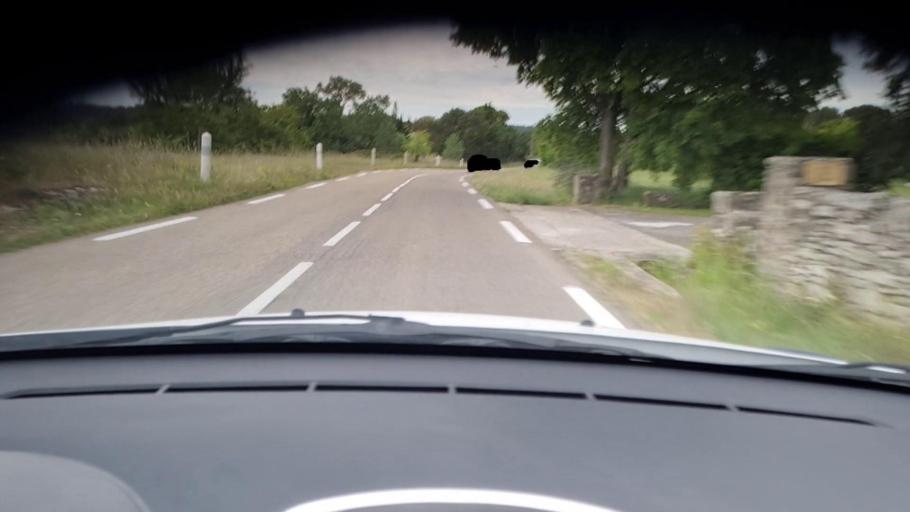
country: FR
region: Languedoc-Roussillon
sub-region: Departement du Gard
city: Uzes
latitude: 43.9943
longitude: 4.4130
